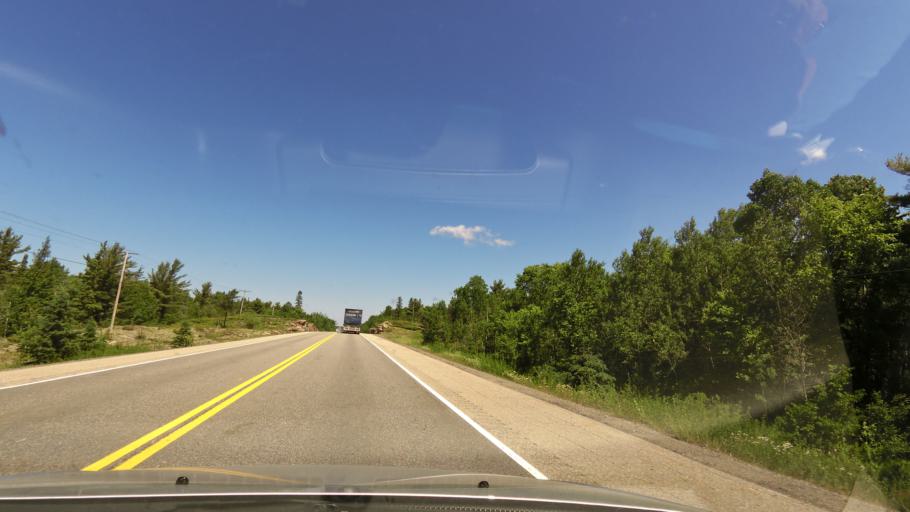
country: CA
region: Ontario
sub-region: Parry Sound District
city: Parry Sound
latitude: 45.8557
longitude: -80.5628
